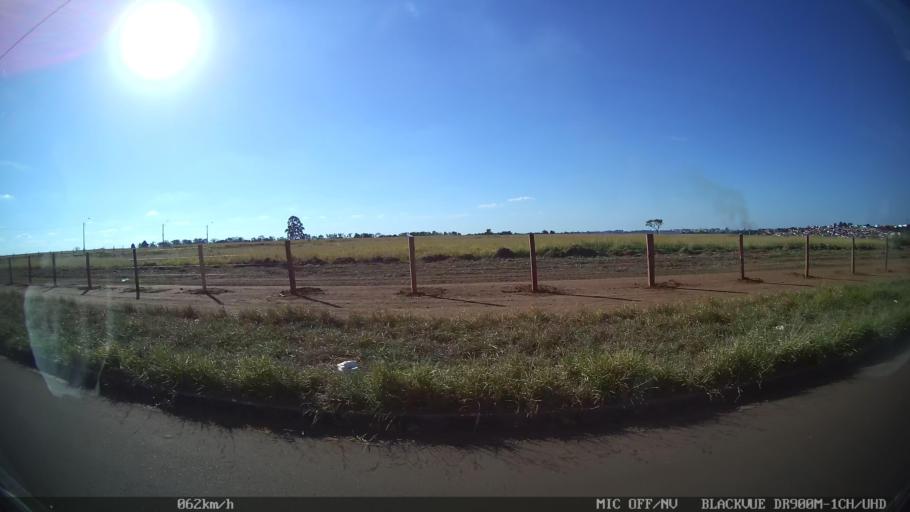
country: BR
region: Sao Paulo
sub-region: Franca
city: Franca
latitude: -20.5061
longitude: -47.4326
